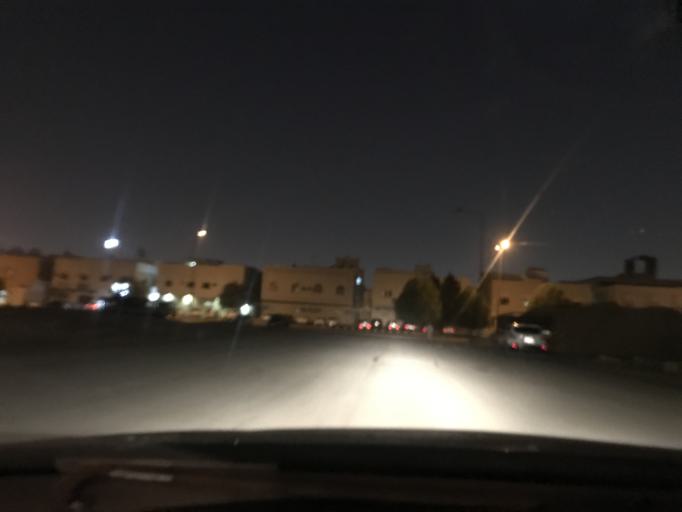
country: SA
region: Ar Riyad
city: Riyadh
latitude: 24.7486
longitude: 46.7581
